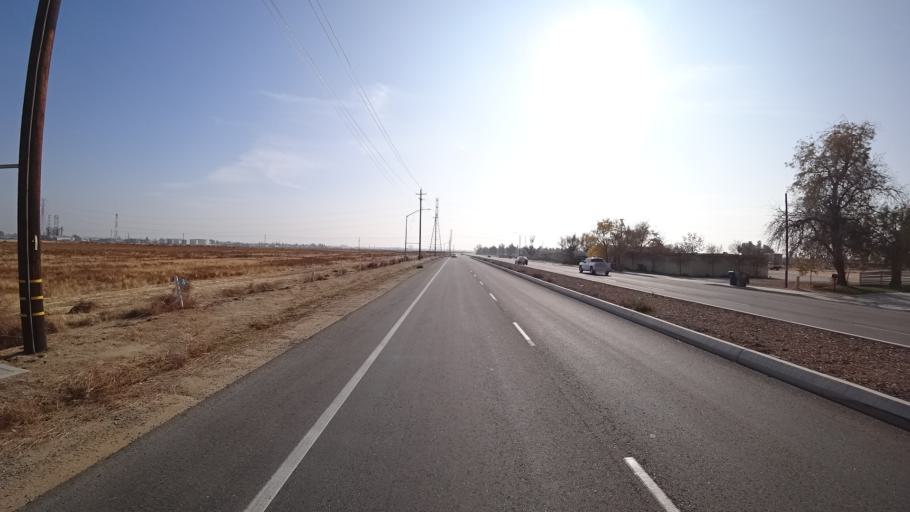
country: US
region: California
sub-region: Kern County
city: Greenacres
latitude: 35.4003
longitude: -119.0653
